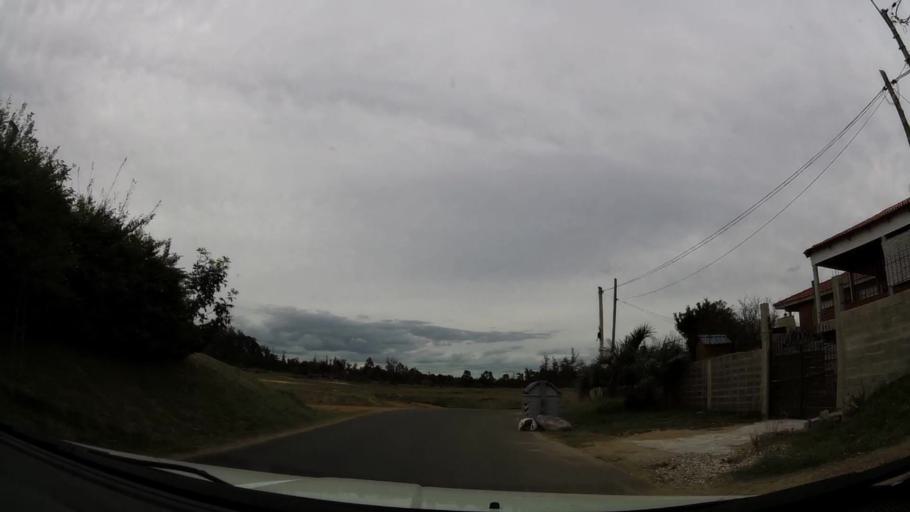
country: UY
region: Maldonado
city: Maldonado
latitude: -34.9042
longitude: -54.9737
